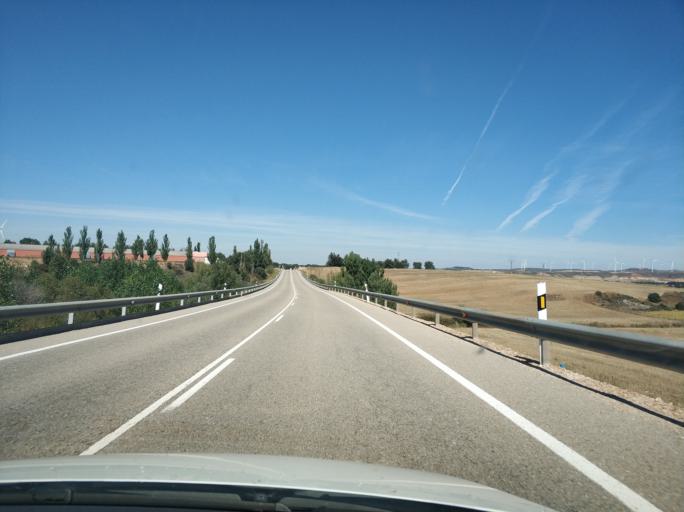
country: ES
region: Castille and Leon
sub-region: Provincia de Burgos
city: Hontoria de la Cantera
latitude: 42.2074
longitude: -3.6494
